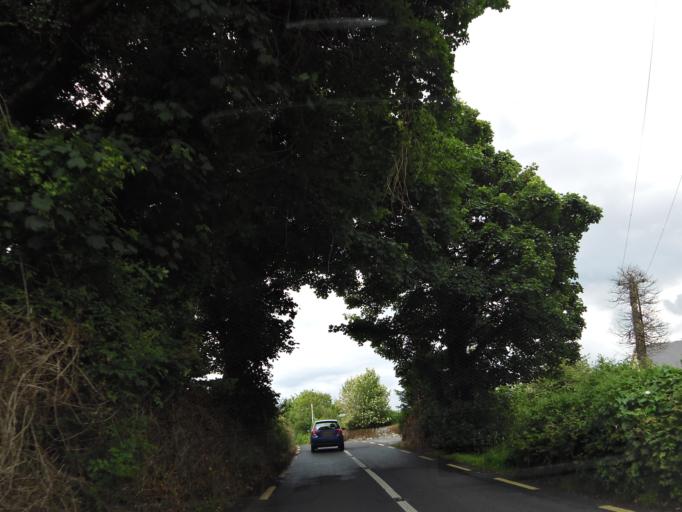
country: IE
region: Connaught
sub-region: County Galway
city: Bearna
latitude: 53.0907
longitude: -9.1730
